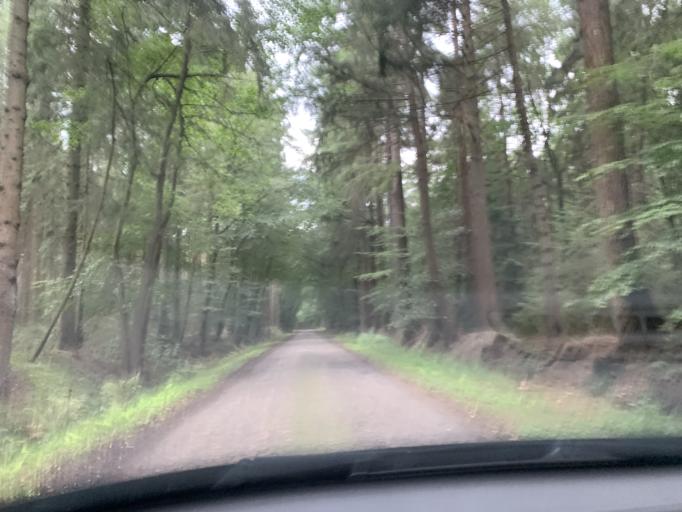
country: DE
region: Lower Saxony
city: Westerstede
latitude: 53.2684
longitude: 7.9963
